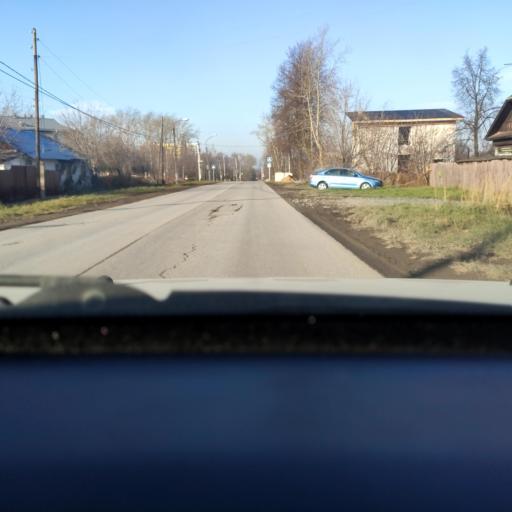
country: RU
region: Perm
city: Perm
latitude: 58.0910
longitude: 56.3869
